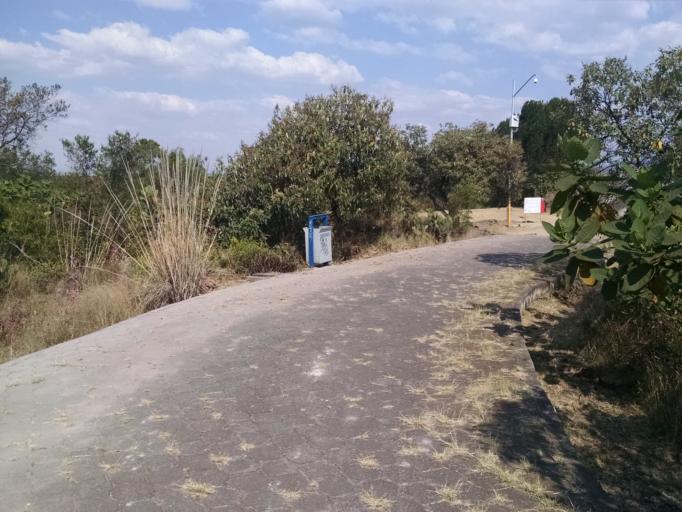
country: MX
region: Mexico City
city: Tlalpan
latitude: 19.3187
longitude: -99.1830
